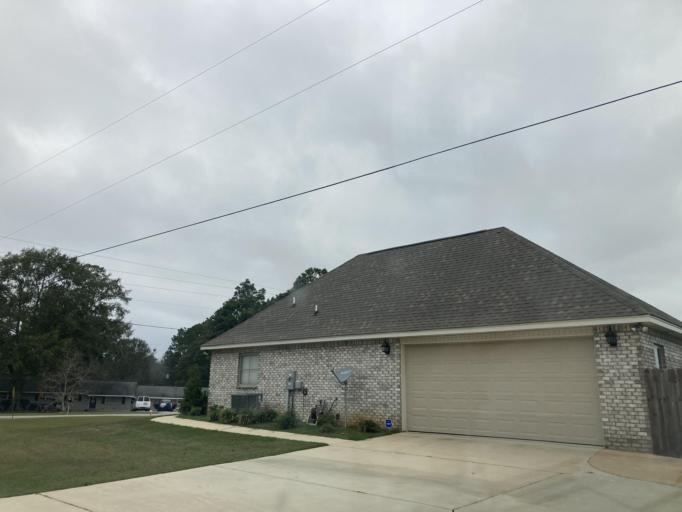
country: US
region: Mississippi
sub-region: Lamar County
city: Purvis
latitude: 31.1473
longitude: -89.4321
